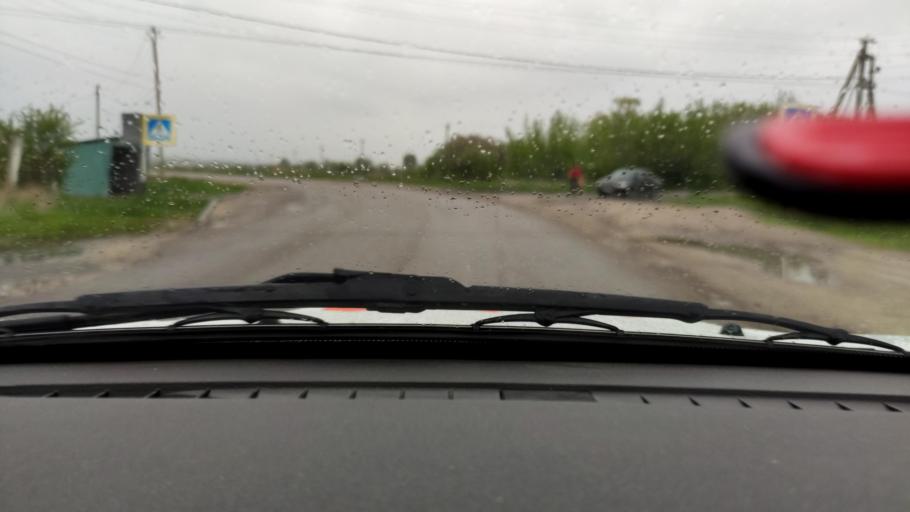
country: RU
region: Voronezj
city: Devitsa
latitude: 51.6311
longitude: 38.9281
